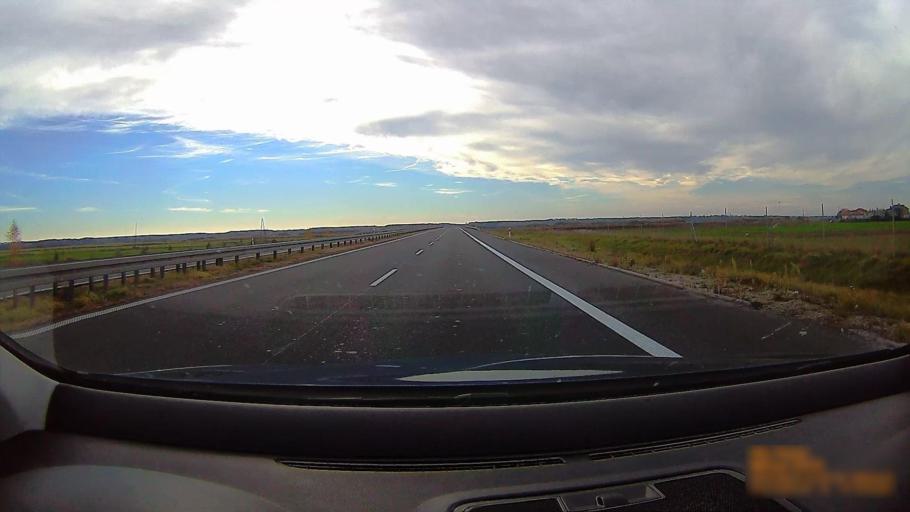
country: PL
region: Greater Poland Voivodeship
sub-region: Powiat ostrowski
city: Przygodzice
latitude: 51.5908
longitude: 17.8500
